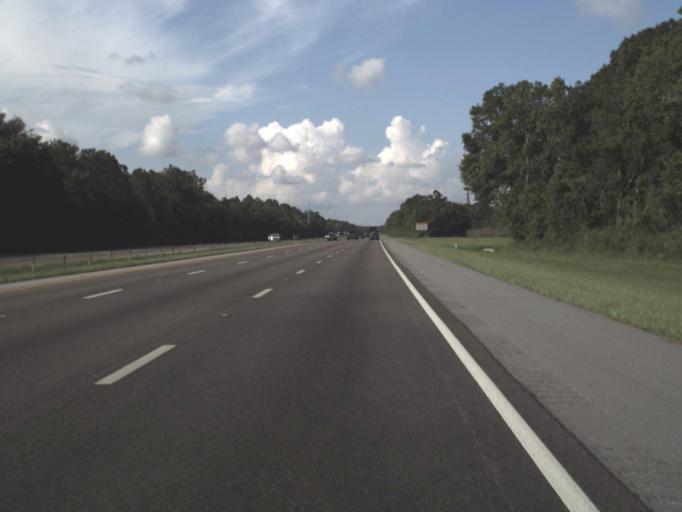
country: US
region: Florida
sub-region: Hillsborough County
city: Lutz
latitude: 28.1364
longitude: -82.4129
